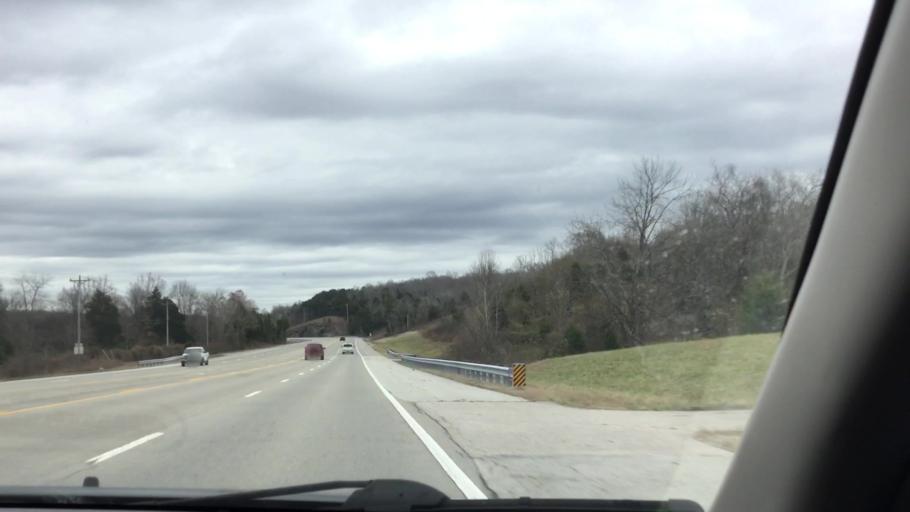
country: US
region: Tennessee
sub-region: Lewis County
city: Hohenwald
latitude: 35.5823
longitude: -87.4417
